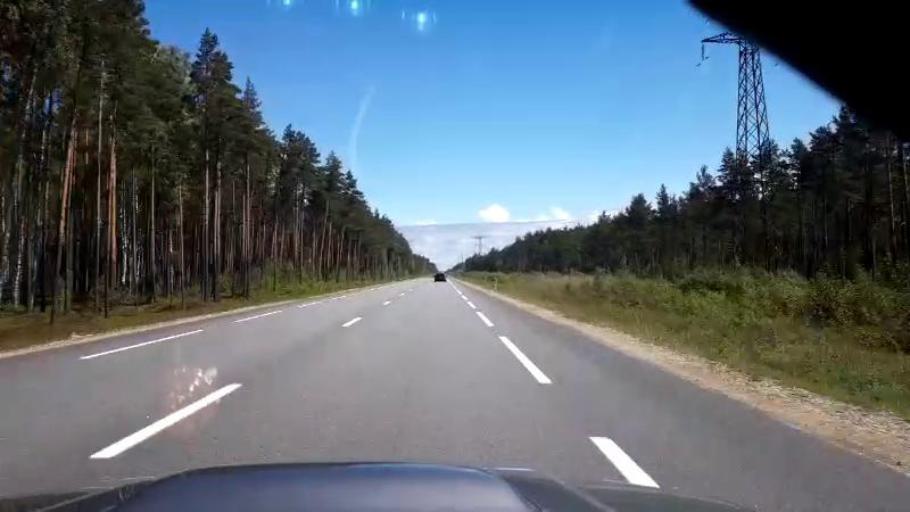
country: LV
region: Saulkrastu
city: Saulkrasti
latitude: 57.2007
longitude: 24.3752
